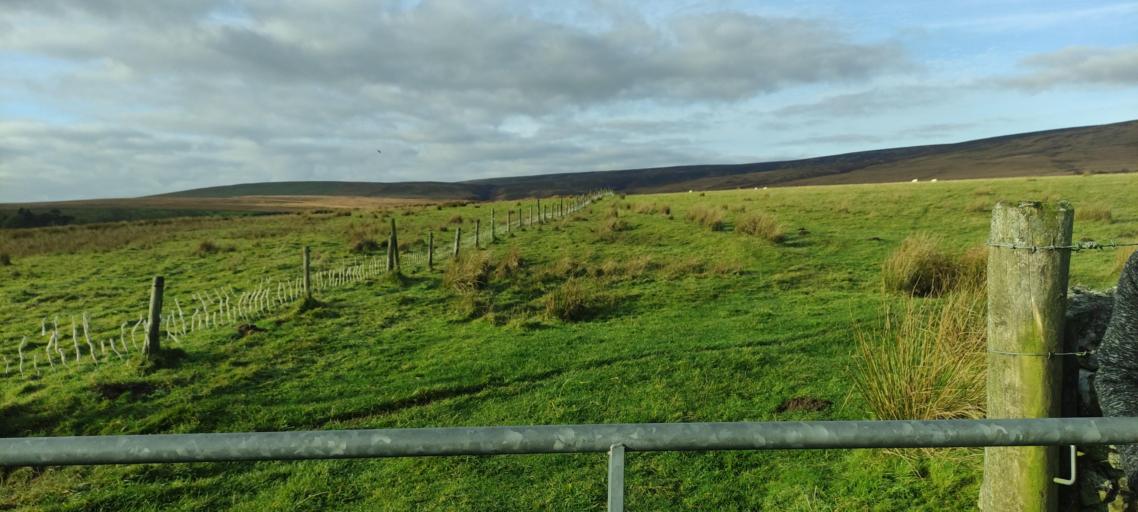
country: GB
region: Scotland
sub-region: Dumfries and Galloway
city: Langholm
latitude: 55.1936
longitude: -2.8205
